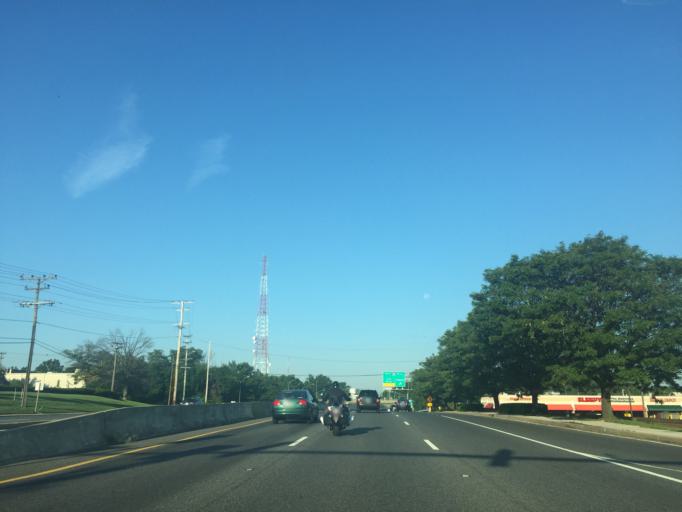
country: US
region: Maryland
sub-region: Baltimore County
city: Catonsville
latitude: 39.2876
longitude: -76.7341
